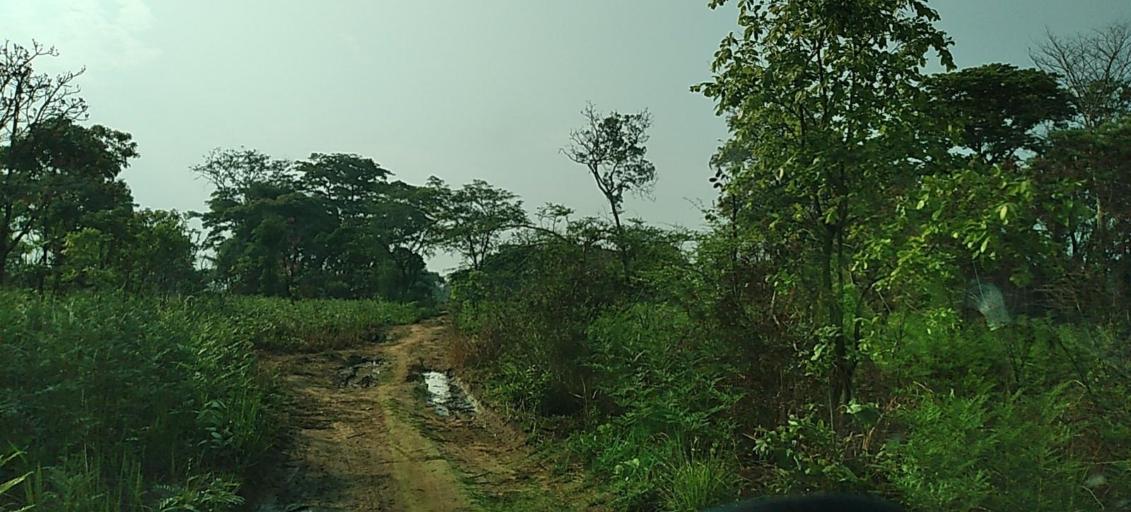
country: ZM
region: North-Western
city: Solwezi
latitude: -12.3978
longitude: 26.5832
